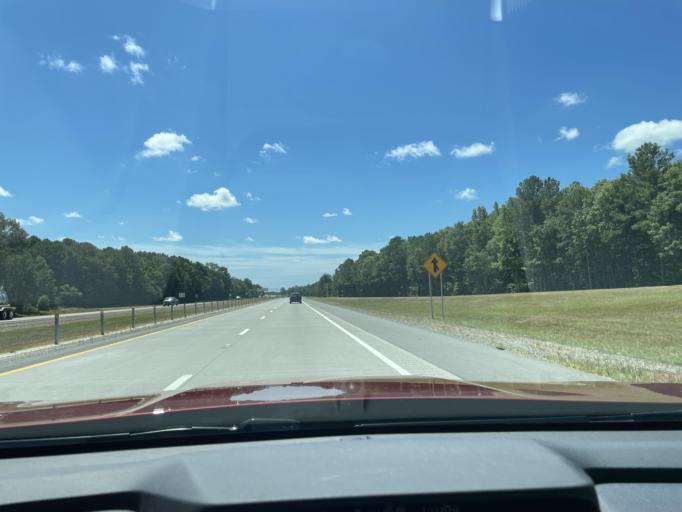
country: US
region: Arkansas
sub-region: Jefferson County
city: White Hall
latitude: 34.2411
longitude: -92.0896
